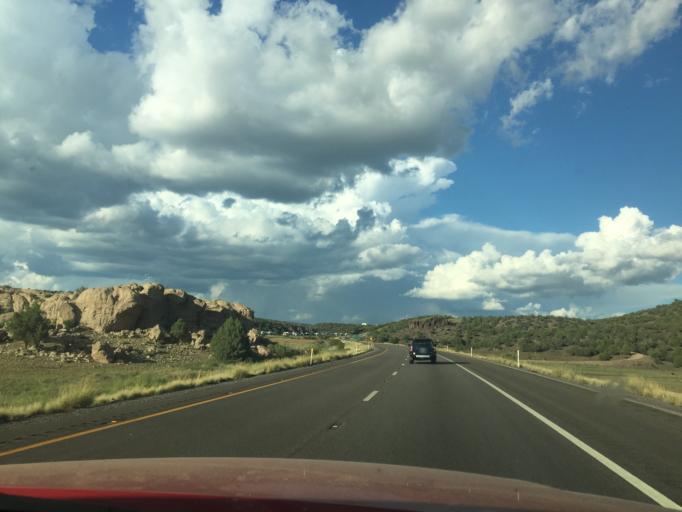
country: US
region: Arizona
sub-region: Mohave County
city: Peach Springs
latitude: 35.1829
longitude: -113.4524
